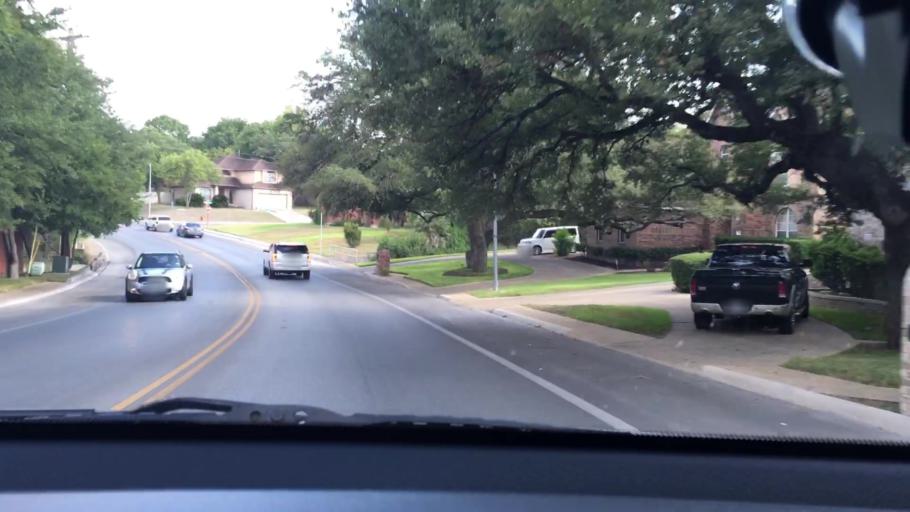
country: US
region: Texas
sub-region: Bexar County
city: Live Oak
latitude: 29.5724
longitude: -98.3210
